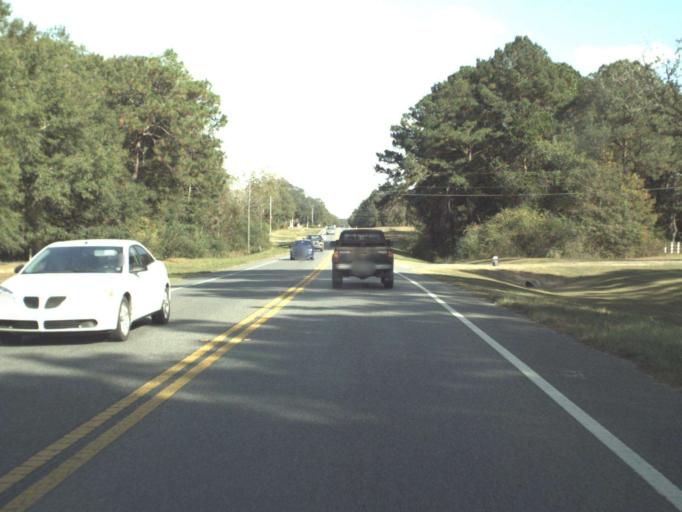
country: US
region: Florida
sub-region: Washington County
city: Chipley
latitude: 30.7761
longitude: -85.5819
